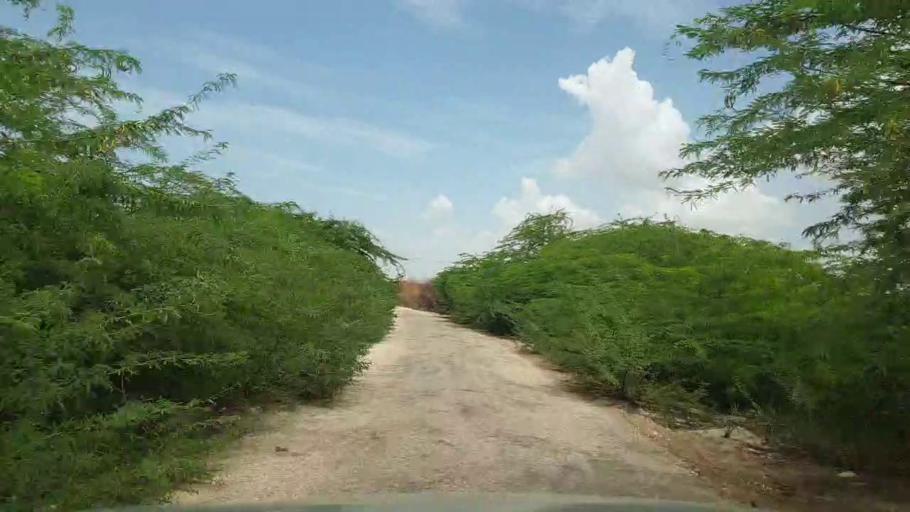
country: PK
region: Sindh
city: Bozdar
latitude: 27.0276
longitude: 68.9545
